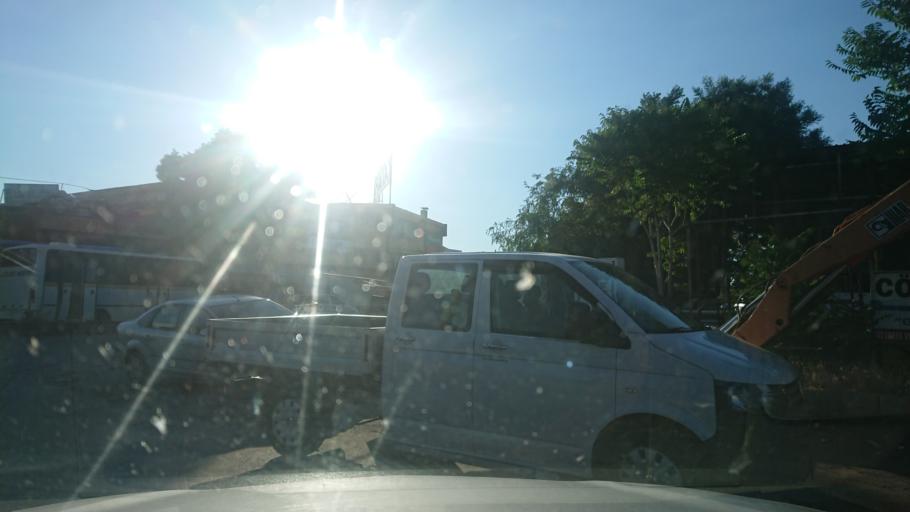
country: TR
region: Aksaray
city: Aksaray
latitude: 38.3724
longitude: 33.9967
